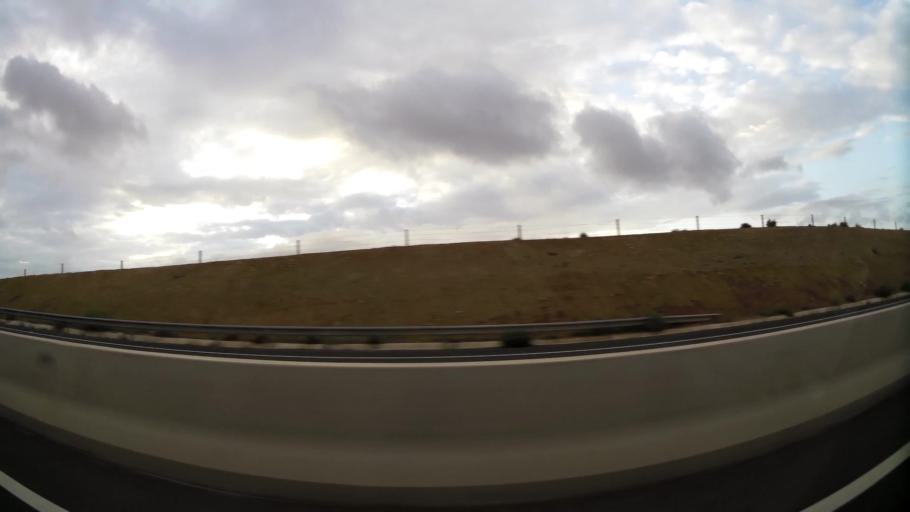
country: MA
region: Oriental
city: Taourirt
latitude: 34.4329
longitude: -3.0924
